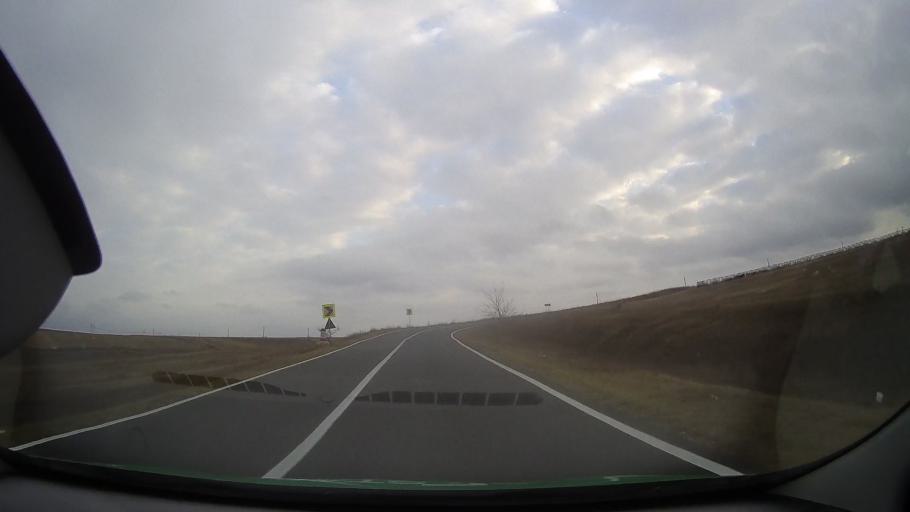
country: RO
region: Constanta
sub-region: Comuna Deleni
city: Deleni
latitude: 44.0942
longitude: 28.0170
